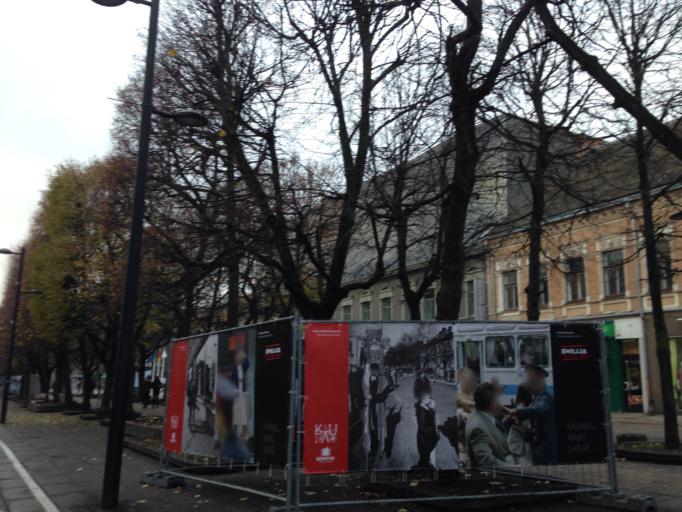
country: LT
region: Kauno apskritis
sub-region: Kaunas
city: Kaunas
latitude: 54.8977
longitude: 23.9079
